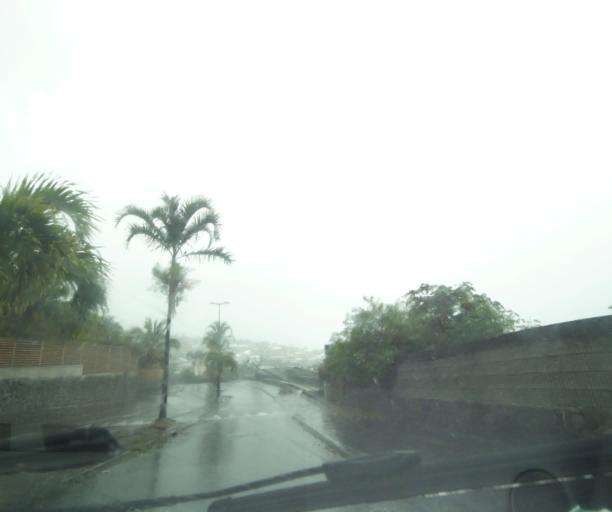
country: RE
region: Reunion
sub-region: Reunion
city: Saint-Paul
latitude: -20.9905
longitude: 55.3281
